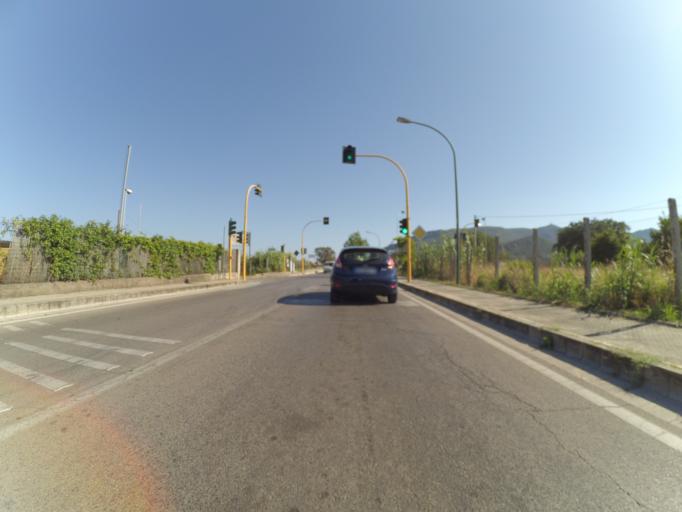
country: IT
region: Latium
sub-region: Provincia di Latina
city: San Felice Circeo
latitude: 41.2525
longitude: 13.0934
